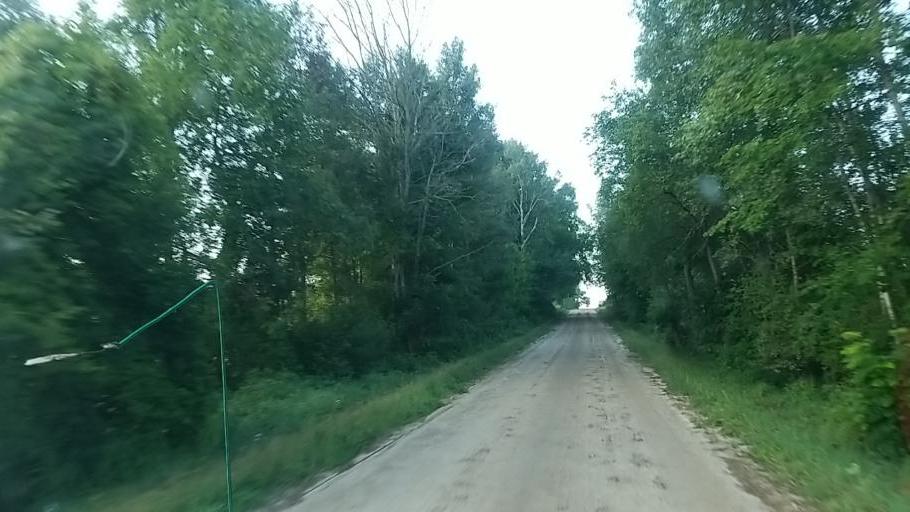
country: US
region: Michigan
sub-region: Osceola County
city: Evart
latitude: 43.9134
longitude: -85.1681
